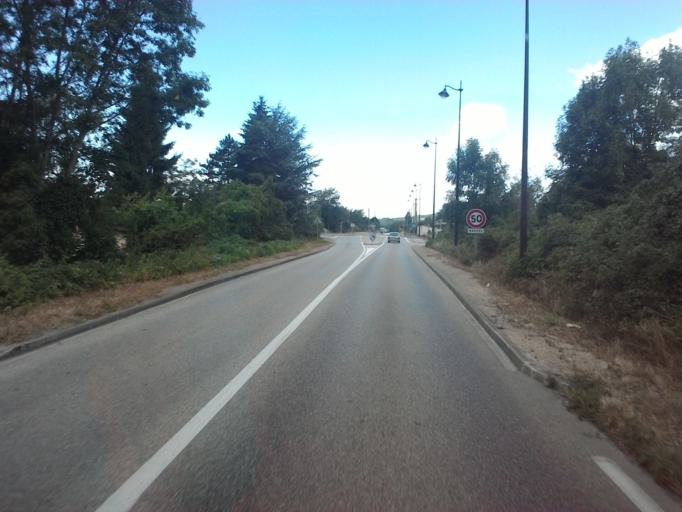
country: FR
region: Rhone-Alpes
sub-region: Departement de l'Ain
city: Saint-Sorlin-en-Bugey
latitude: 45.8725
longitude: 5.3645
